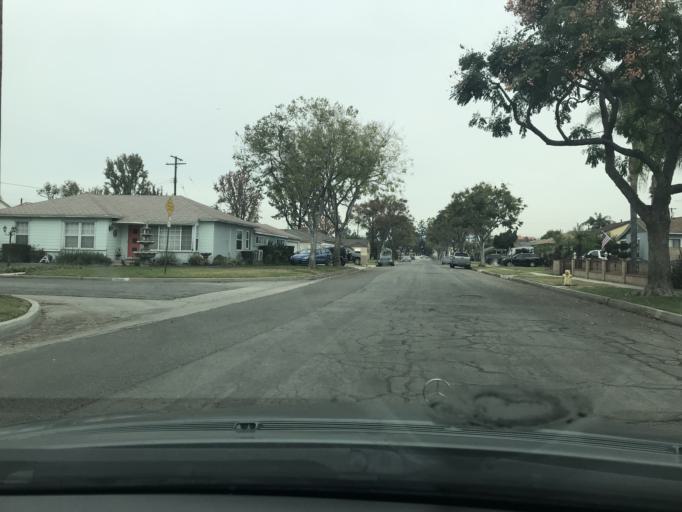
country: US
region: California
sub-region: Los Angeles County
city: Santa Fe Springs
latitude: 33.9327
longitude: -118.0889
